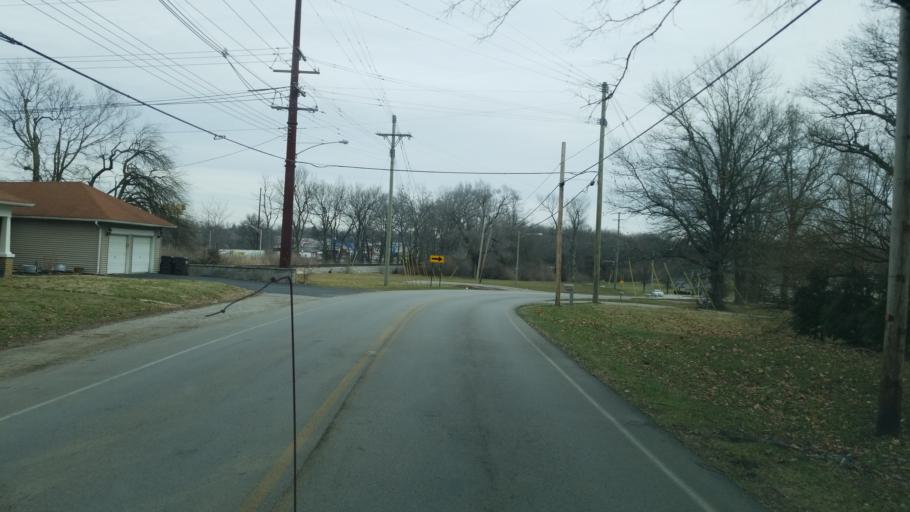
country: US
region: Kentucky
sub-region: Fayette County
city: Lexington-Fayette
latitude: 38.0767
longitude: -84.4534
